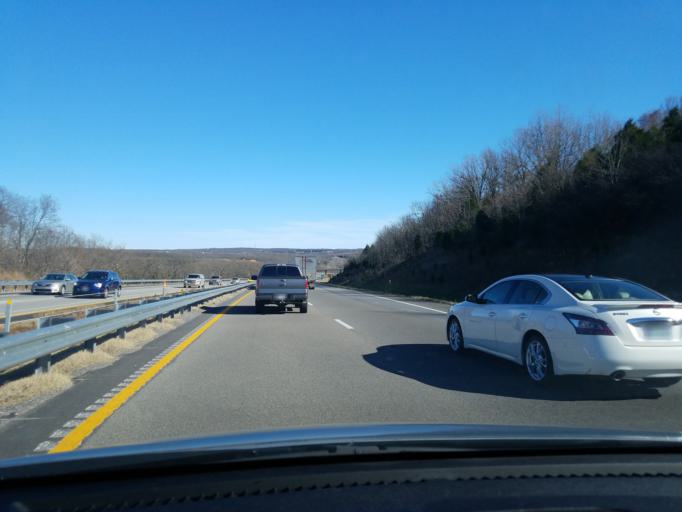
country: US
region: Missouri
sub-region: Webster County
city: Marshfield
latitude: 37.3021
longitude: -93.0067
